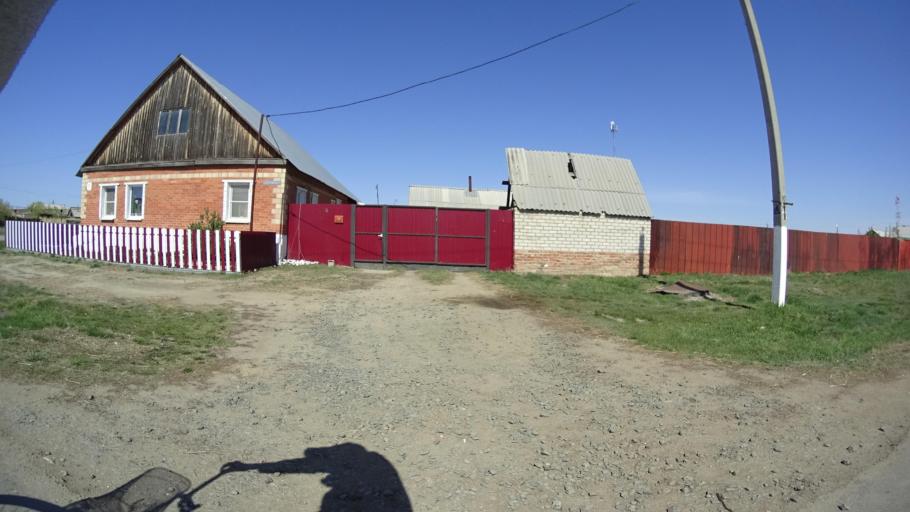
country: RU
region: Chelyabinsk
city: Chesma
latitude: 53.7939
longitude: 61.0339
